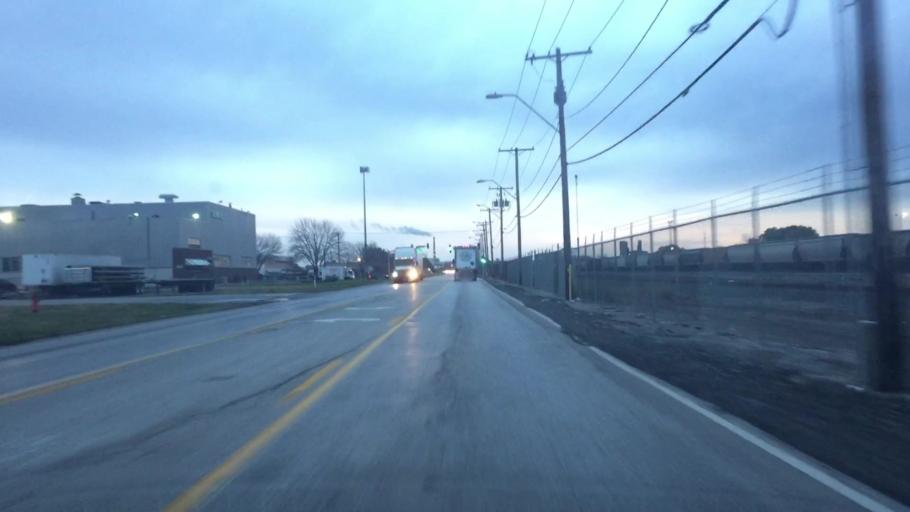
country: US
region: Missouri
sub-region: Clay County
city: North Kansas City
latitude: 39.1311
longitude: -94.5339
